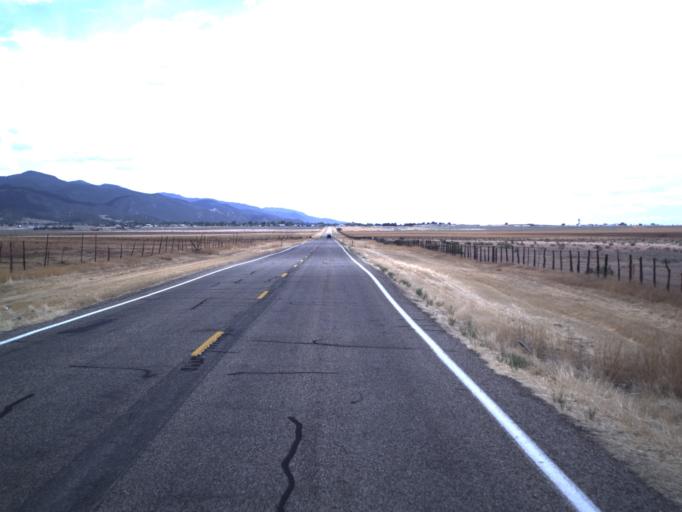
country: US
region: Utah
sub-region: Iron County
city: Parowan
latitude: 37.8717
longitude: -112.7928
